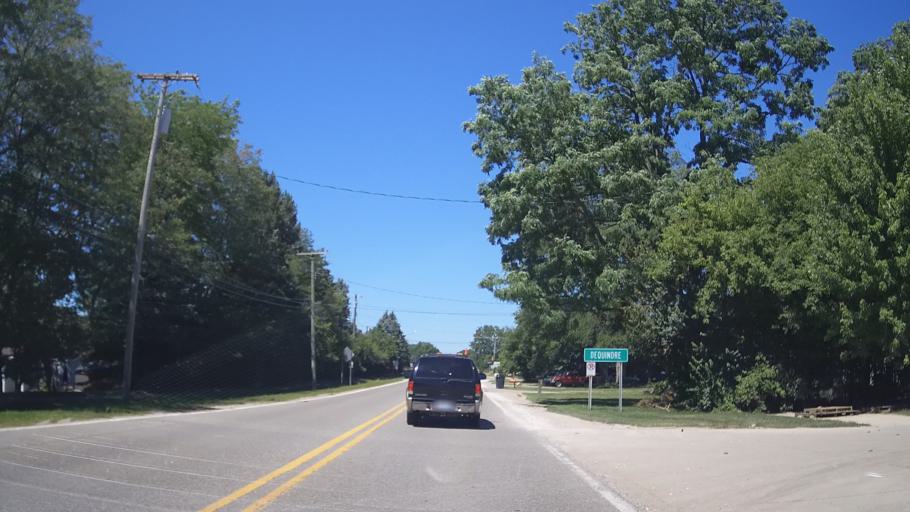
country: US
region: Michigan
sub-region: Oakland County
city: Rochester
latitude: 42.6534
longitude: -83.0899
